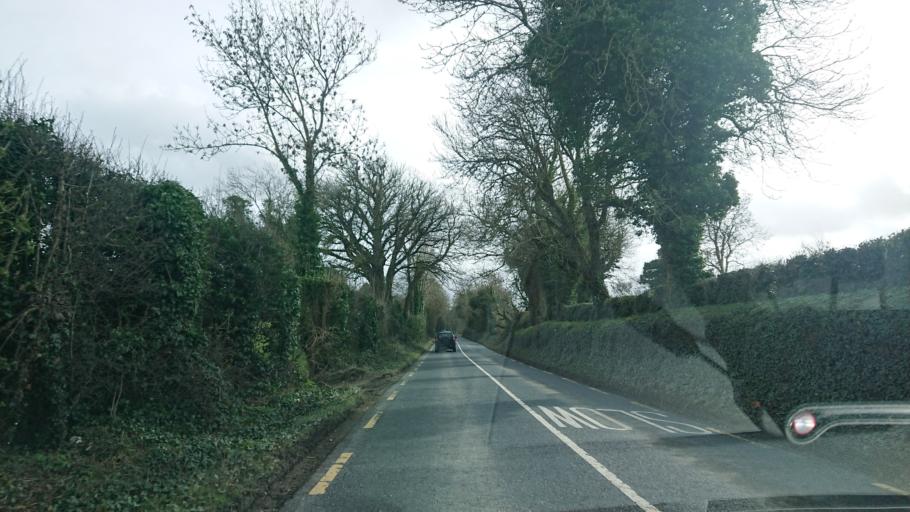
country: IE
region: Leinster
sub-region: Kildare
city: Eadestown
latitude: 53.1934
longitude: -6.5611
